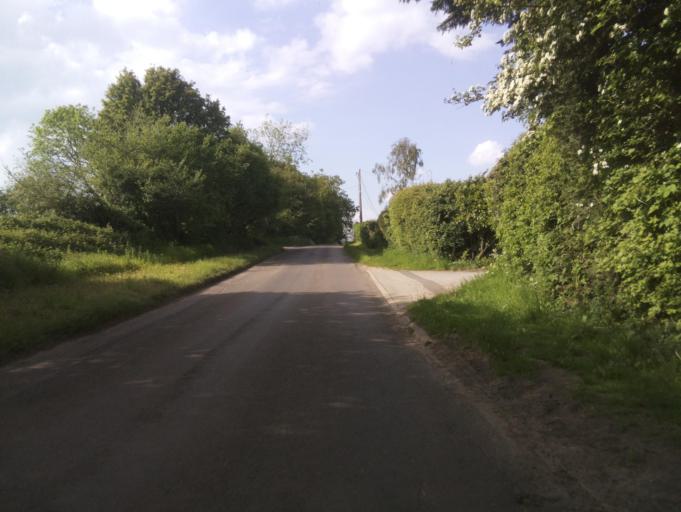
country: GB
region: England
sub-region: Wiltshire
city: Malmesbury
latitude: 51.5179
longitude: -2.0751
